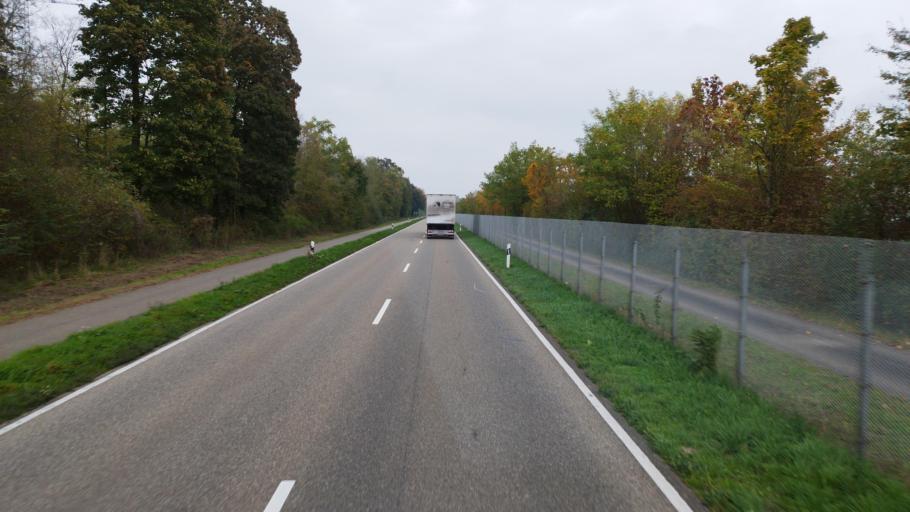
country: DE
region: Baden-Wuerttemberg
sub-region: Karlsruhe Region
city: Rheinau
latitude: 48.8641
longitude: 8.1733
